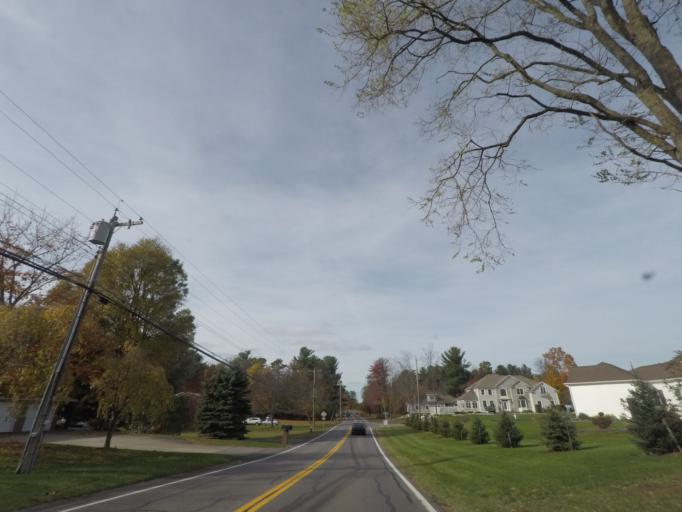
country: US
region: New York
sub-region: Schenectady County
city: Rotterdam
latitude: 42.7476
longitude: -73.9315
